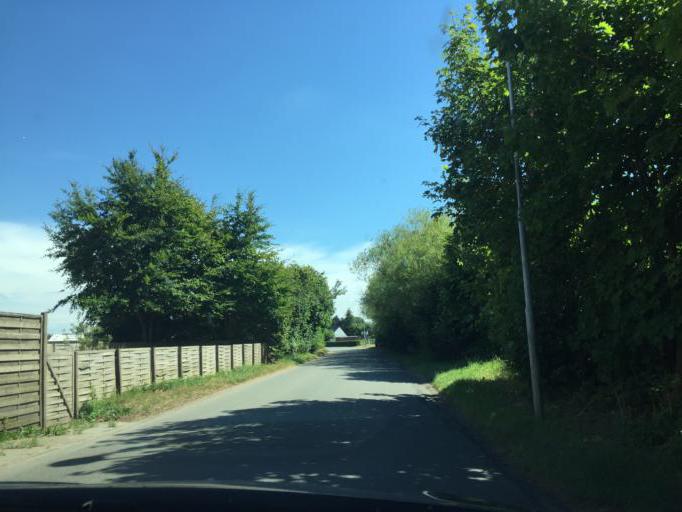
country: DK
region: South Denmark
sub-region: Odense Kommune
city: Bellinge
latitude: 55.3109
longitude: 10.3204
